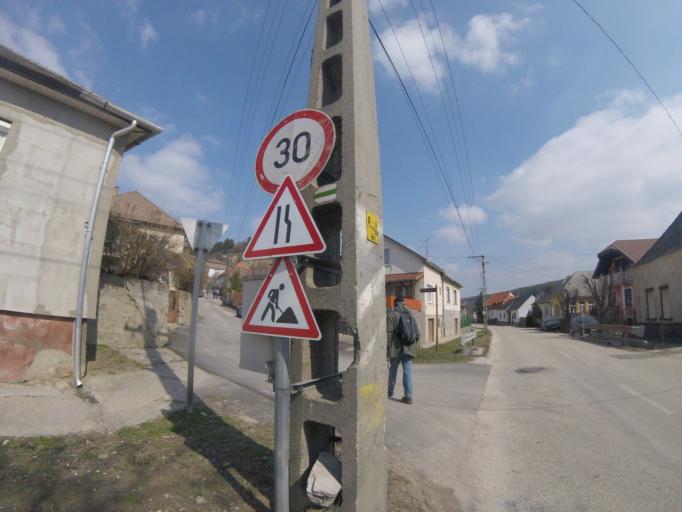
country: HU
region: Komarom-Esztergom
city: Nyergesujfalu
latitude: 47.7590
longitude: 18.5560
